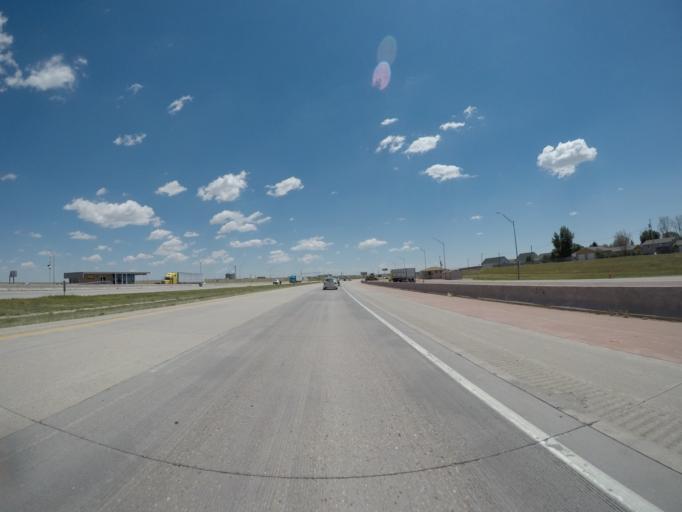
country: US
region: Colorado
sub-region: Lincoln County
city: Limon
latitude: 39.2733
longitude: -103.6868
